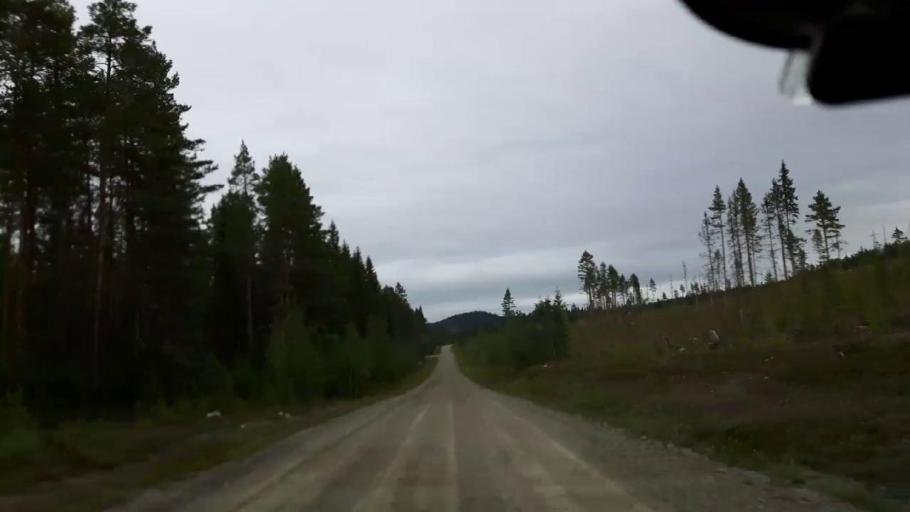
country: SE
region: Vaesternorrland
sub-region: Ange Kommun
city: Fransta
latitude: 62.8617
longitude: 16.0434
